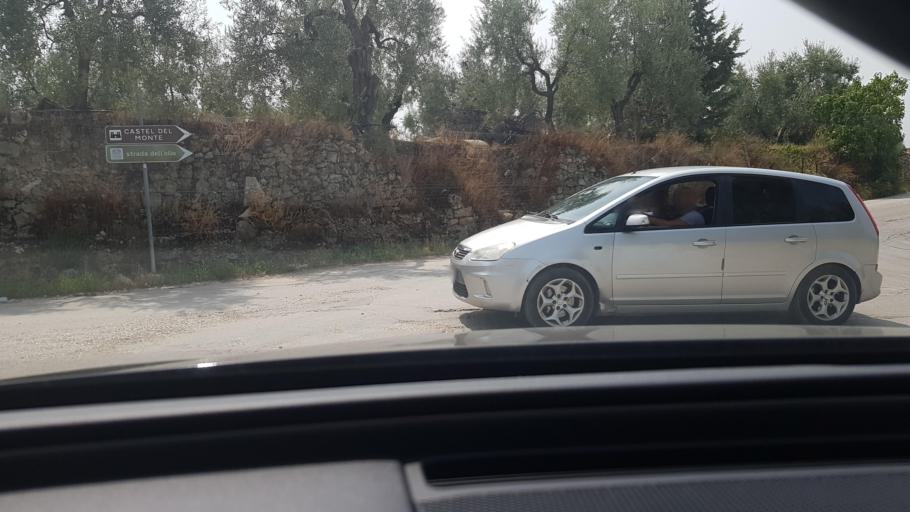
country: IT
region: Apulia
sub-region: Provincia di Barletta - Andria - Trani
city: Andria
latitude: 41.2263
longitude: 16.2683
